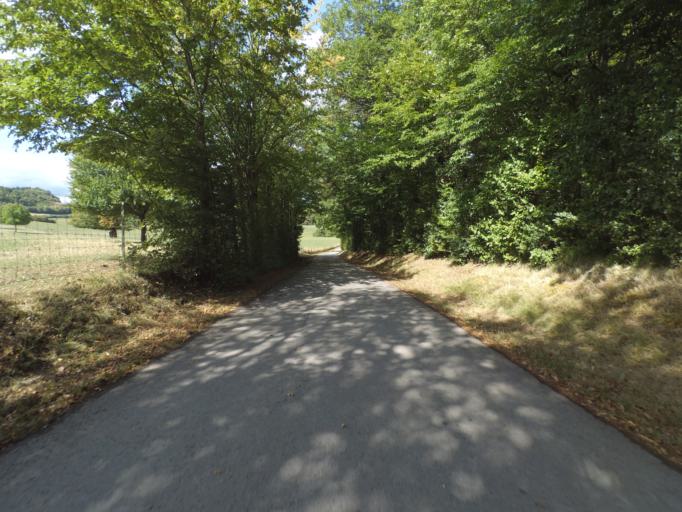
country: LU
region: Grevenmacher
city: Gonderange
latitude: 49.6811
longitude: 6.2673
